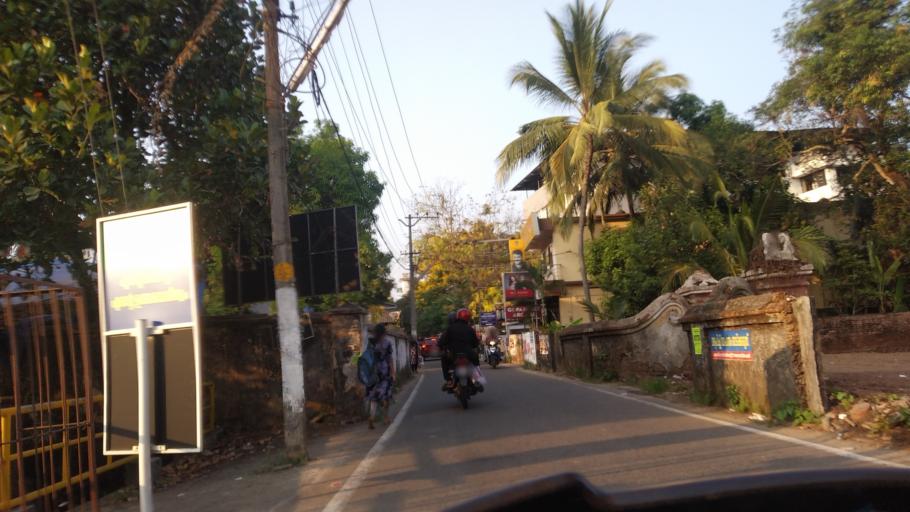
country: IN
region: Kerala
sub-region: Thrissur District
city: Kodungallur
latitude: 10.1475
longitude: 76.2288
